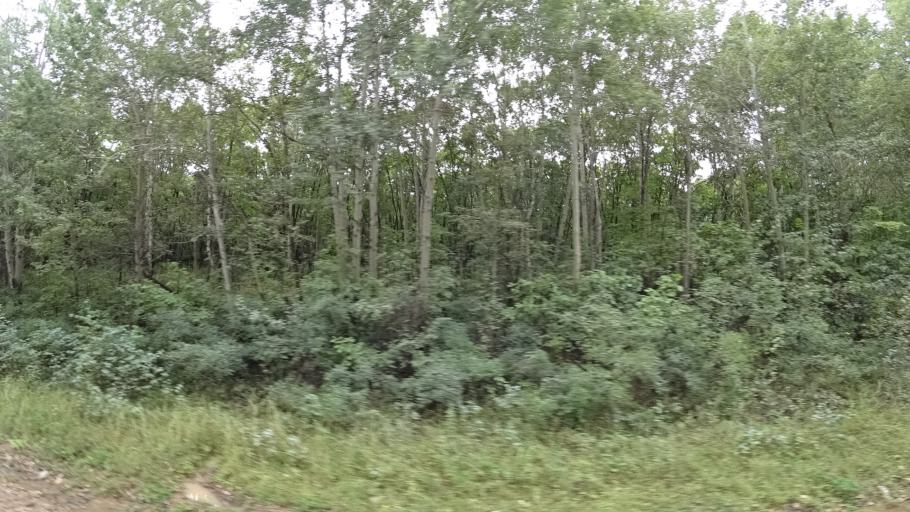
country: RU
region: Primorskiy
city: Lyalichi
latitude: 44.0848
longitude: 132.4426
